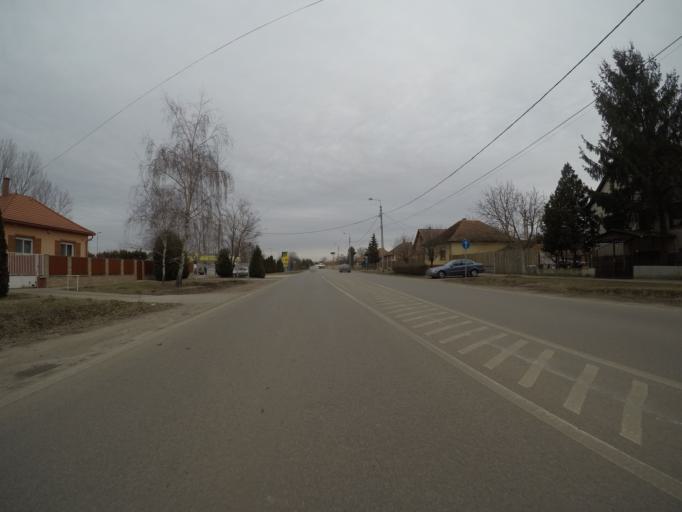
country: HU
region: Jasz-Nagykun-Szolnok
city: Jaszjakohalma
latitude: 47.5227
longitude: 19.9983
